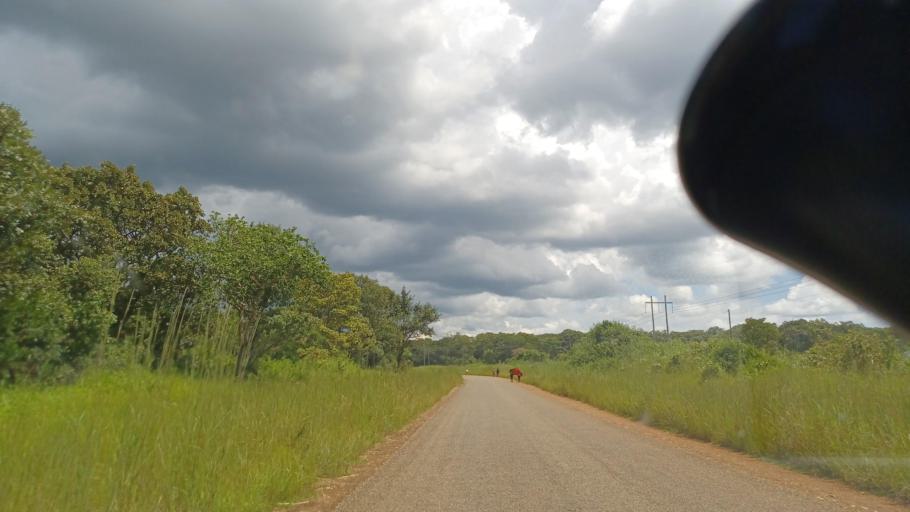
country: ZM
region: North-Western
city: Kasempa
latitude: -12.7779
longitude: 26.0100
